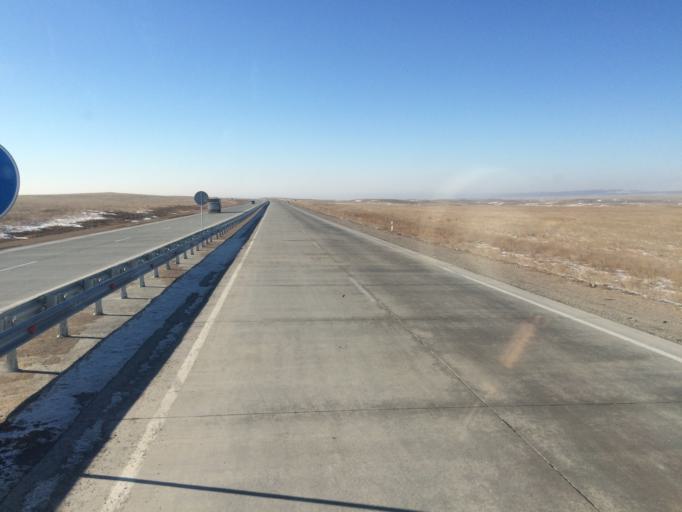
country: KZ
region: Zhambyl
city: Georgiyevka
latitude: 43.3482
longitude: 74.5158
